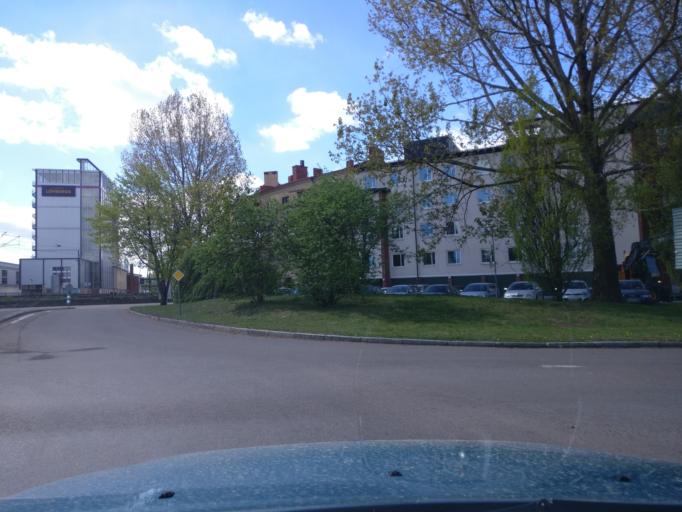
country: SE
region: Vaermland
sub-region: Karlstads Kommun
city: Karlstad
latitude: 59.3789
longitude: 13.5087
